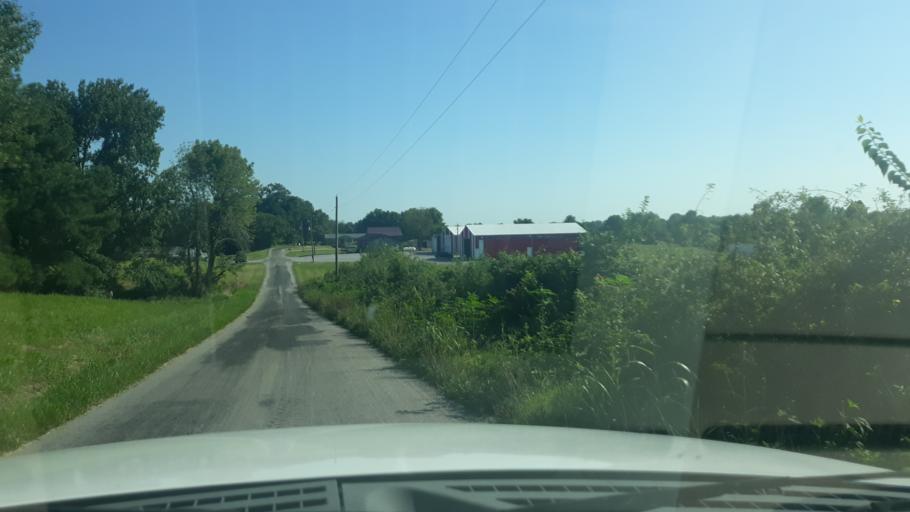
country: US
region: Illinois
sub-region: Saline County
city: Harrisburg
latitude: 37.8497
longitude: -88.6010
